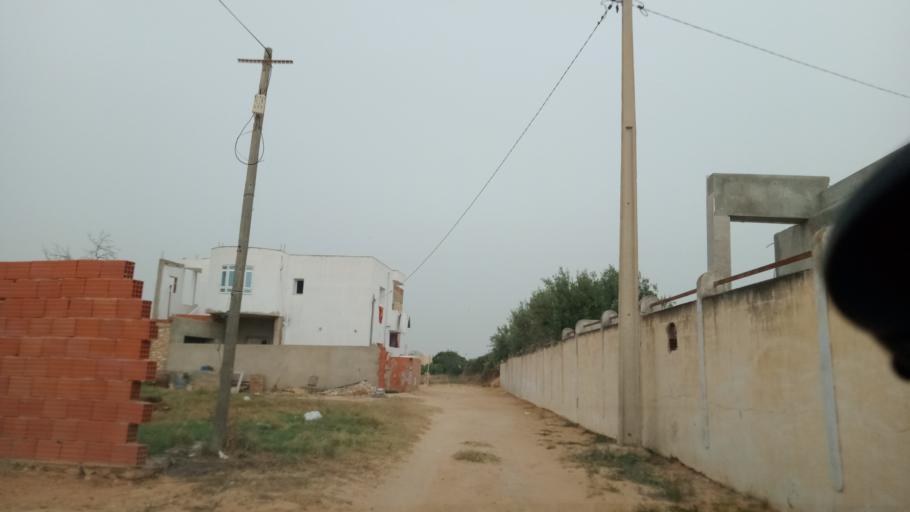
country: TN
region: Safaqis
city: Al Qarmadah
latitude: 34.7961
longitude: 10.7680
